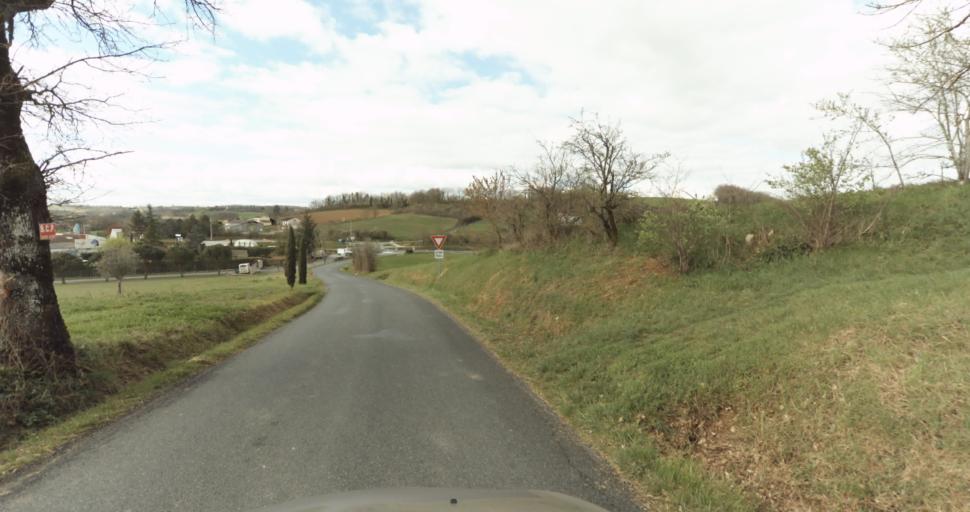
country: FR
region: Midi-Pyrenees
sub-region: Departement du Tarn
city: Puygouzon
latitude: 43.8658
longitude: 2.1890
